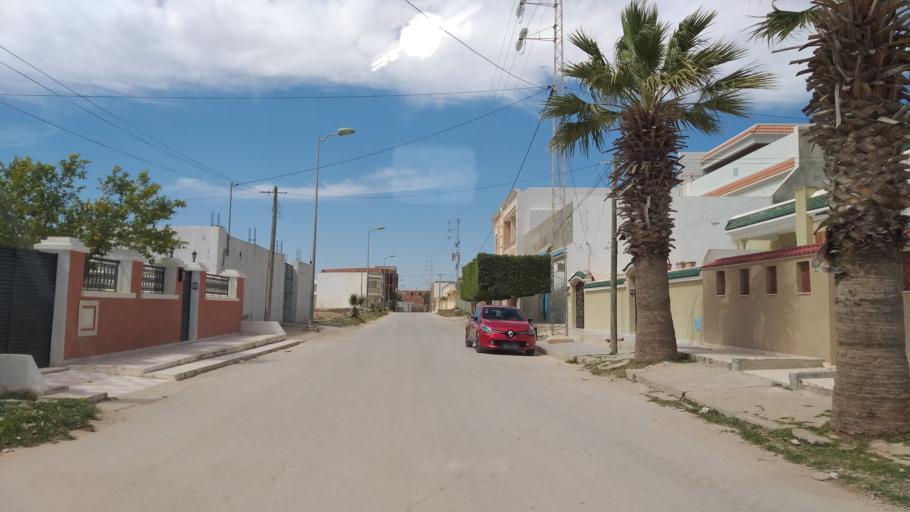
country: TN
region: Al Mahdiyah
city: El Jem
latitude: 35.3009
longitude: 10.7009
